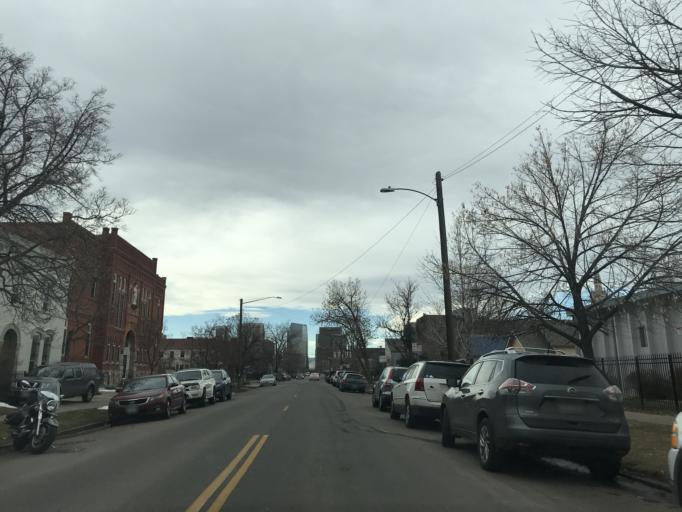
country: US
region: Colorado
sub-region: Denver County
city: Denver
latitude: 39.7606
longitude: -104.9809
